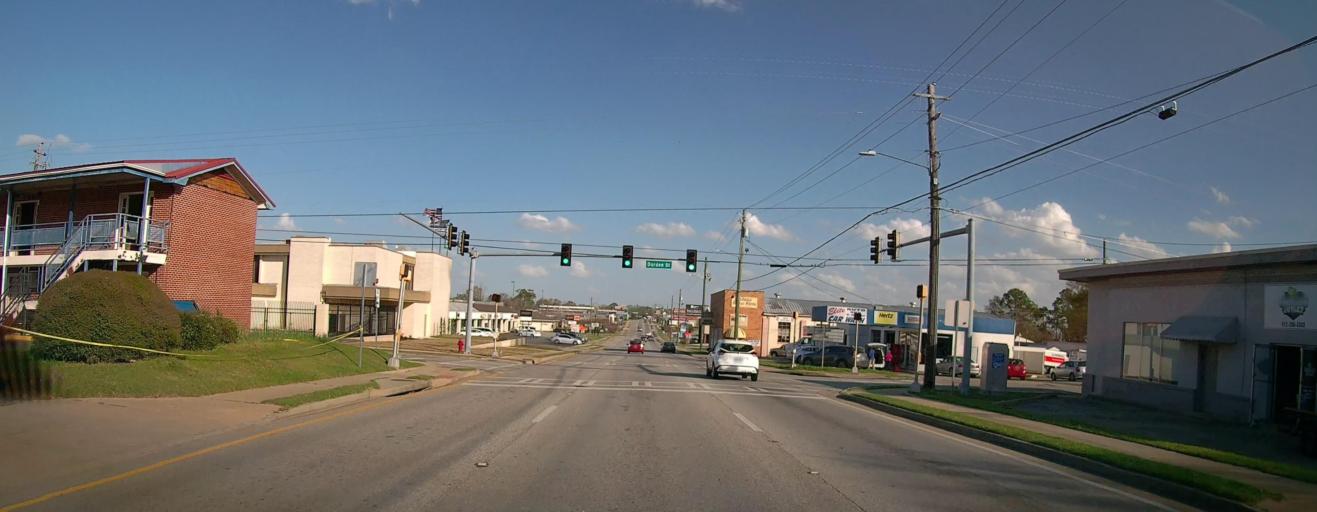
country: US
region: Georgia
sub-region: Toombs County
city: Vidalia
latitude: 32.2165
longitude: -82.4107
